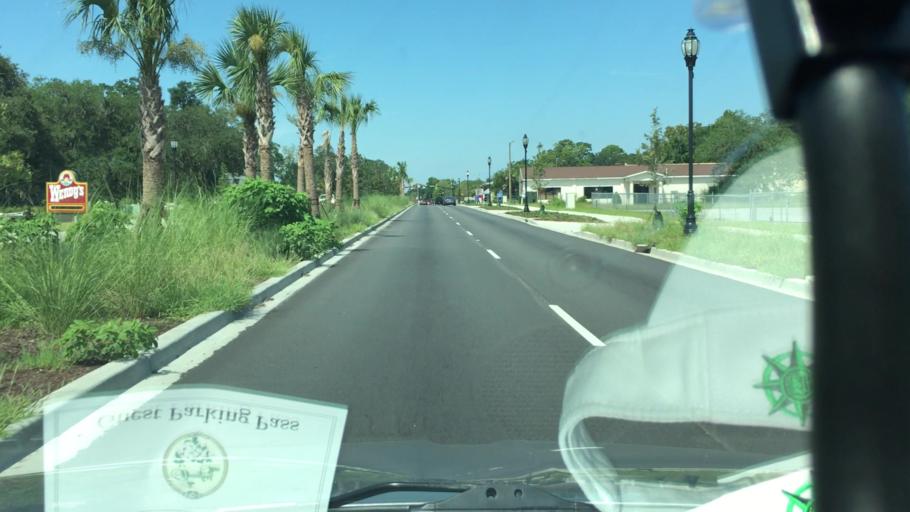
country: US
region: South Carolina
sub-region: Beaufort County
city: Burton
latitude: 32.4415
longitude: -80.6964
